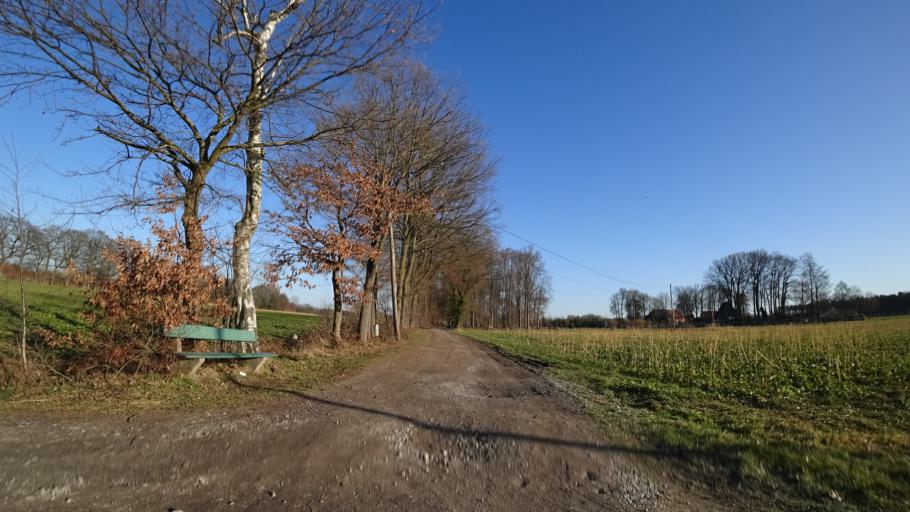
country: DE
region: North Rhine-Westphalia
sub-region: Regierungsbezirk Detmold
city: Guetersloh
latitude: 51.9331
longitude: 8.3274
